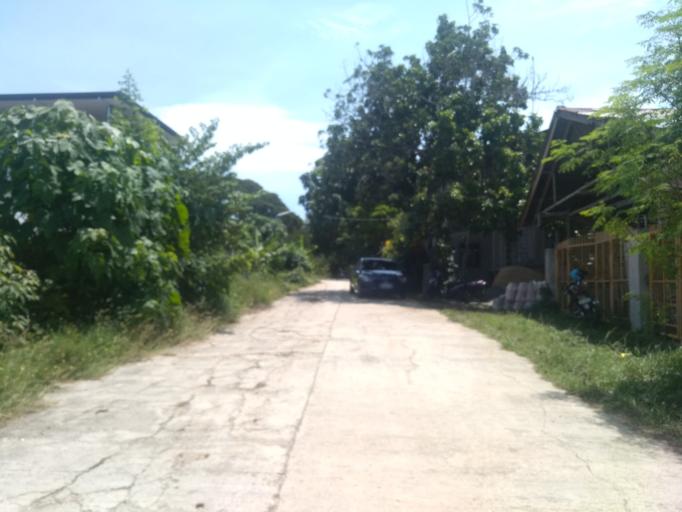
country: PH
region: Central Visayas
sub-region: Province of Siquijor
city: Lazi
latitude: 9.1292
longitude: 123.6336
